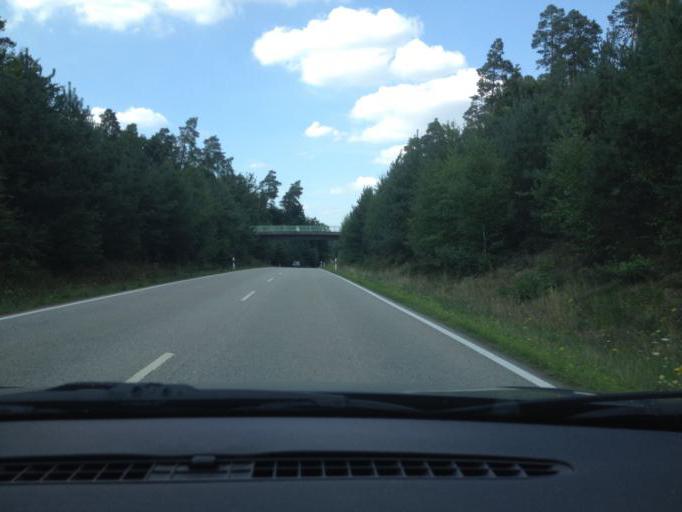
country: DE
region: Rheinland-Pfalz
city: Ramstein-Miesenbach
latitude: 49.4529
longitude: 7.5672
